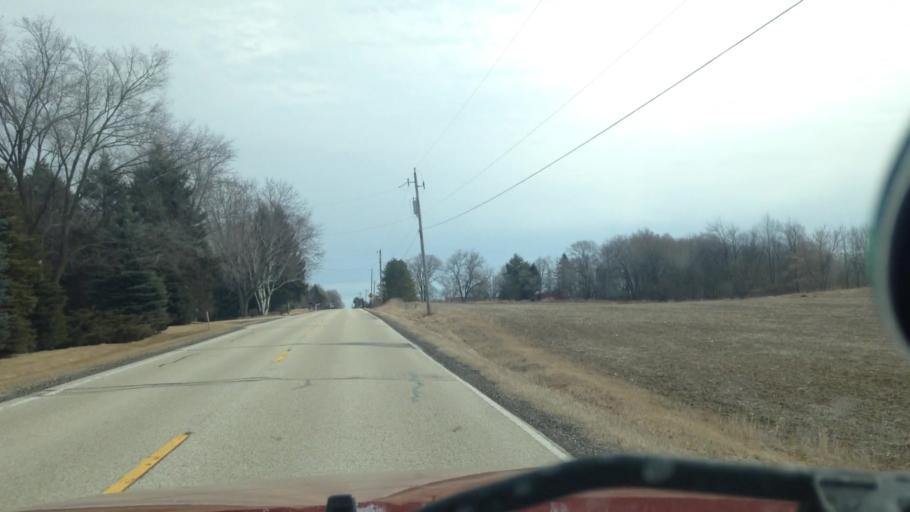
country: US
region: Wisconsin
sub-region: Waukesha County
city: Sussex
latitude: 43.1627
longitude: -88.2180
